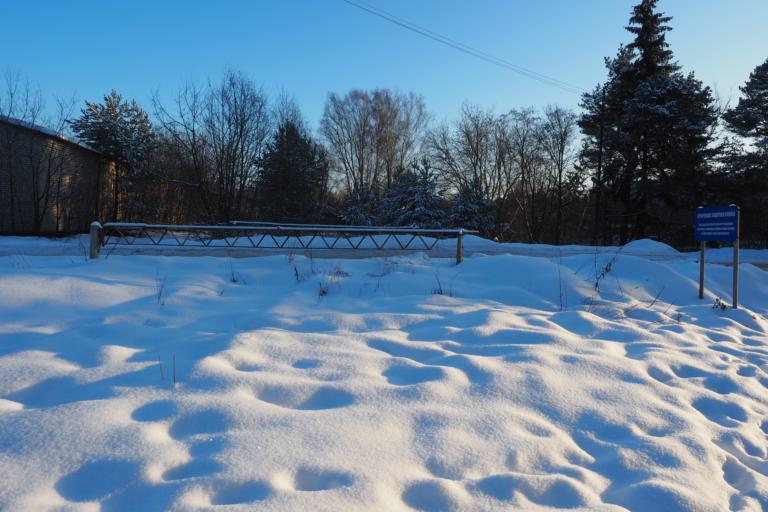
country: RU
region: Tverskaya
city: Ves'yegonsk
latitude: 58.6499
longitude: 37.2651
